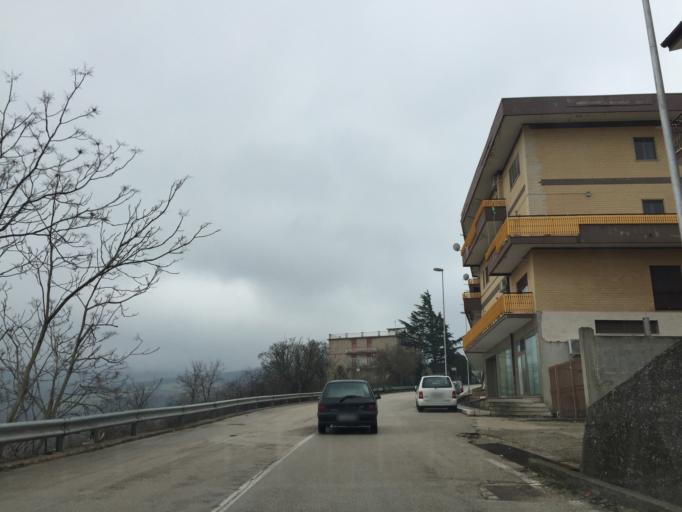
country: IT
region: Apulia
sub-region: Provincia di Foggia
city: Bovino
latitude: 41.2509
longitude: 15.3450
